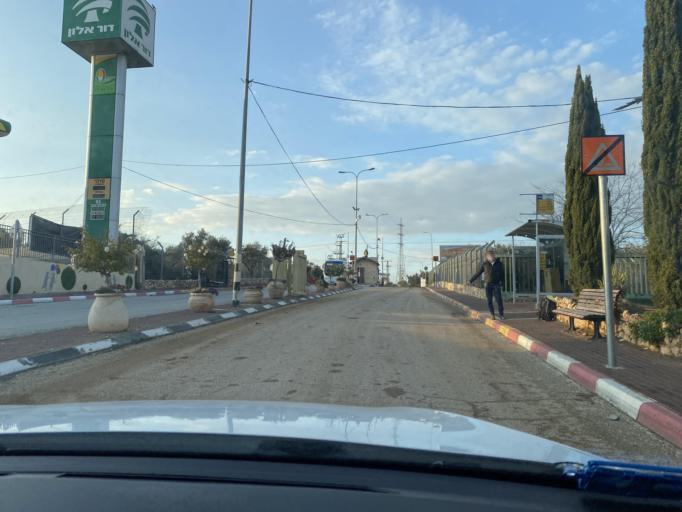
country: PS
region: West Bank
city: Karney Shomron
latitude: 32.1753
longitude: 35.0931
